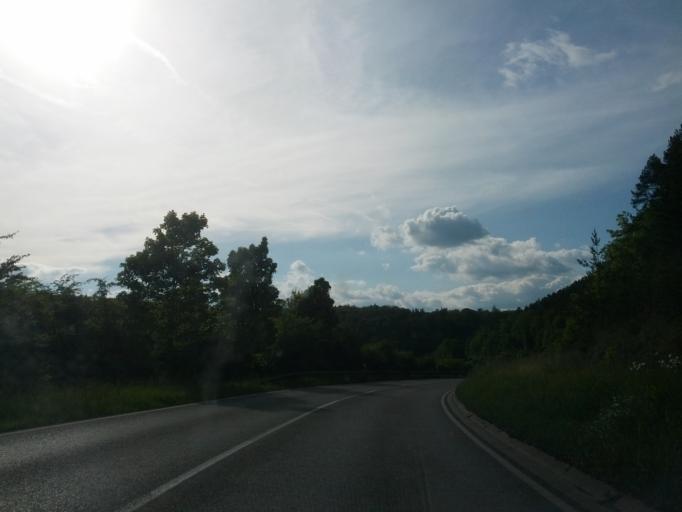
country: DE
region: Baden-Wuerttemberg
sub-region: Regierungsbezirk Stuttgart
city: Aidlingen
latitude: 48.6990
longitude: 8.9239
